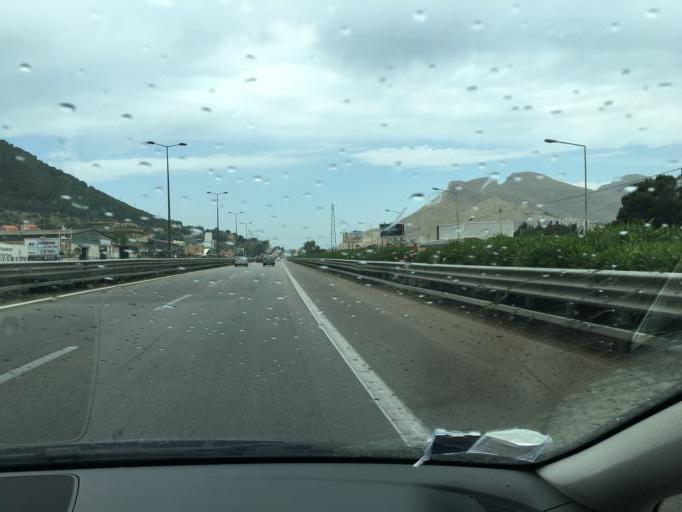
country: IT
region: Sicily
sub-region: Palermo
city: Isola delle Femmine
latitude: 38.1748
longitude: 13.2963
